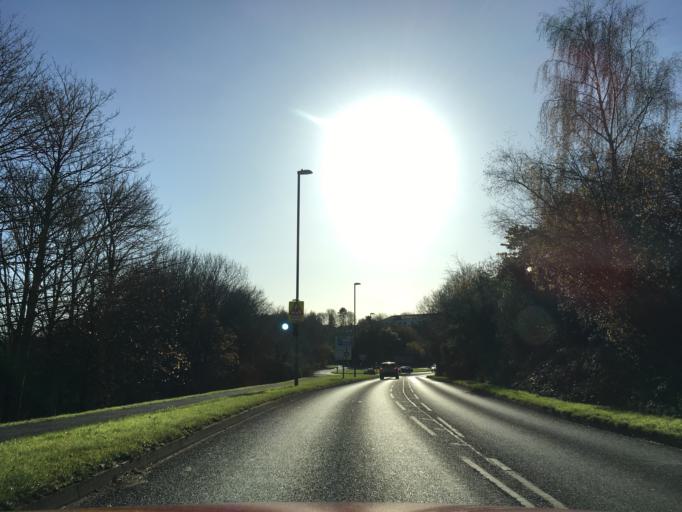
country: GB
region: England
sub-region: Hampshire
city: Compton
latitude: 51.0478
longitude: -1.3434
